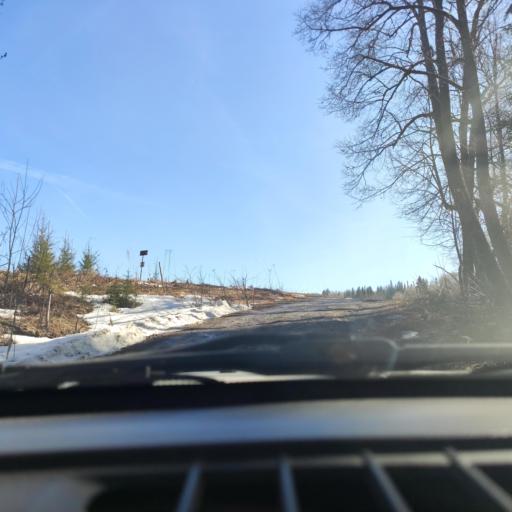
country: RU
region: Perm
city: Kultayevo
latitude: 57.8241
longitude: 55.7881
